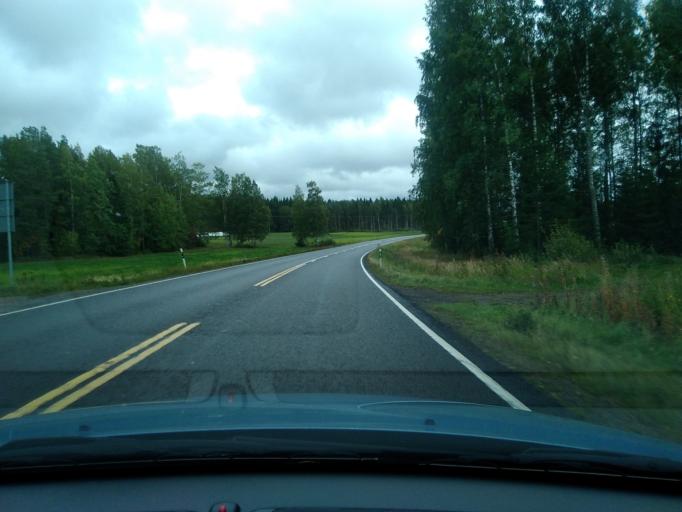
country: FI
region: Central Finland
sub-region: Saarijaervi-Viitasaari
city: Saarijaervi
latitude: 62.6884
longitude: 25.3267
